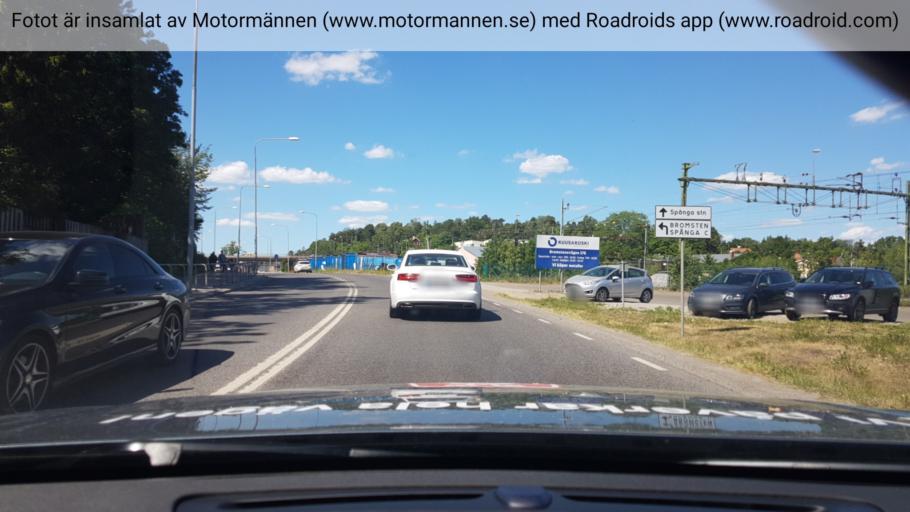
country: SE
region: Stockholm
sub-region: Stockholms Kommun
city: Kista
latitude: 59.3800
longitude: 17.9045
